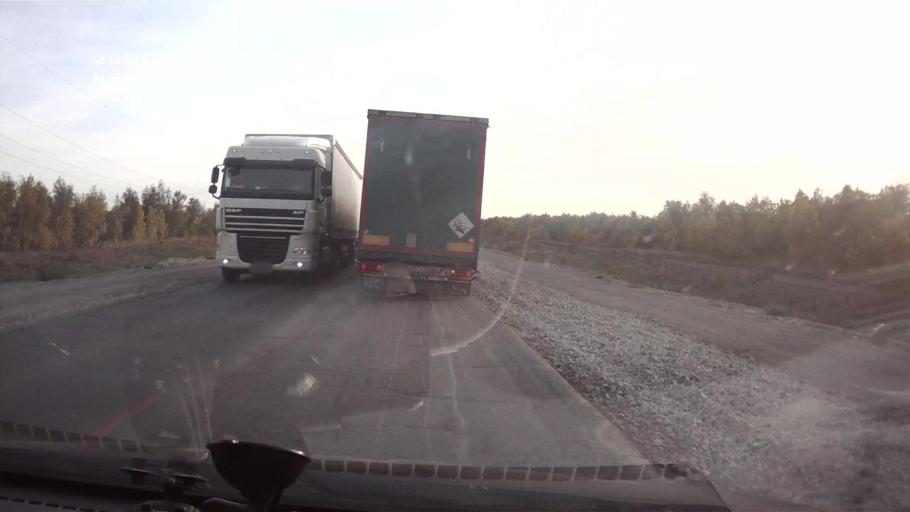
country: RU
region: Saratov
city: Krasnyy Oktyabr'
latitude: 51.3033
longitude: 45.6915
